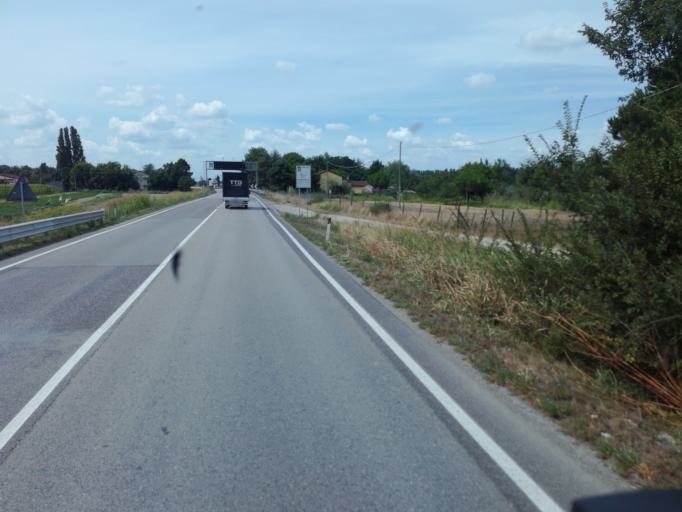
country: IT
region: Emilia-Romagna
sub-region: Provincia di Ferrara
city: Bosco Mesola
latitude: 44.8790
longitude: 12.2009
